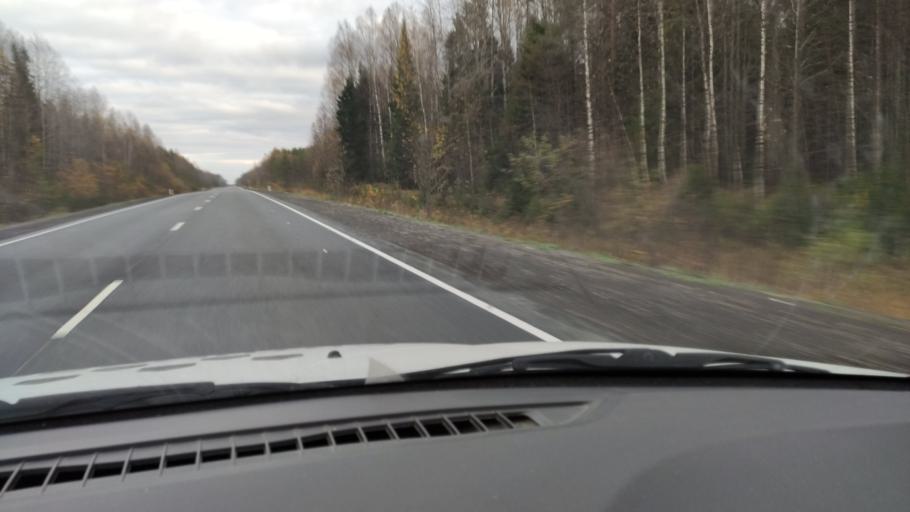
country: RU
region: Kirov
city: Chernaya Kholunitsa
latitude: 58.8816
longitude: 51.4299
